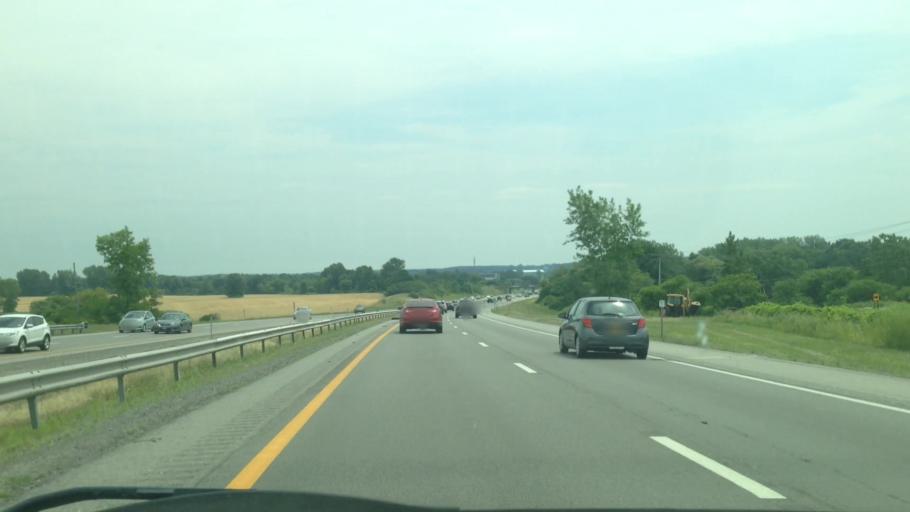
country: US
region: New York
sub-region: Genesee County
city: Batavia
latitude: 43.0208
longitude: -78.1266
